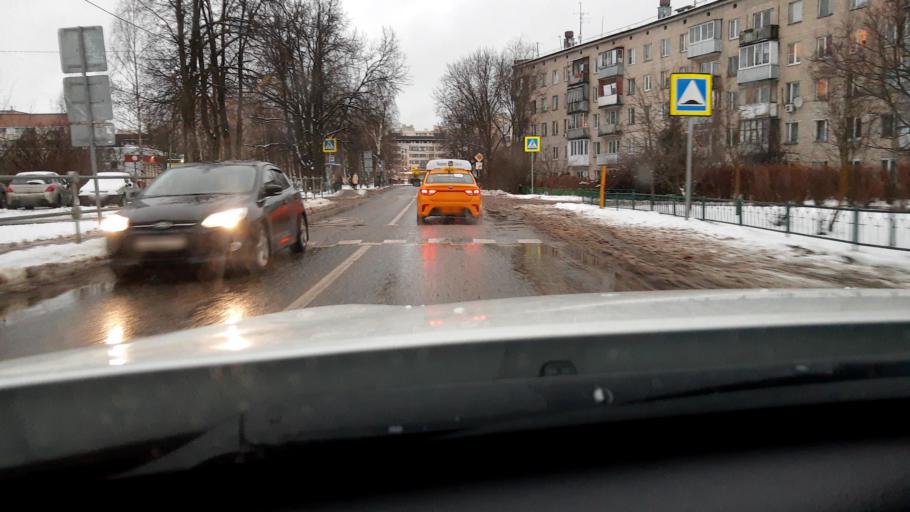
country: RU
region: Moskovskaya
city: Krasnogorsk
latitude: 55.8737
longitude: 37.3110
